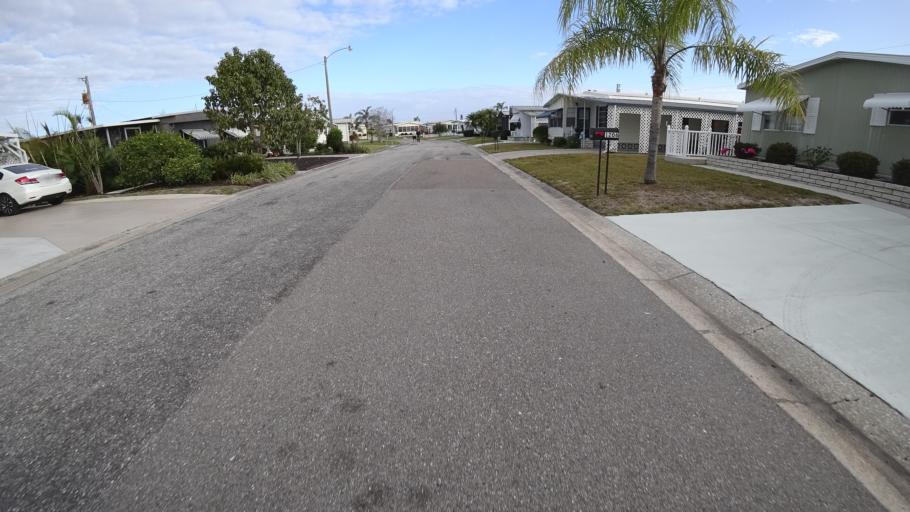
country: US
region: Florida
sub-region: Manatee County
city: Ellenton
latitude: 27.5239
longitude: -82.5187
